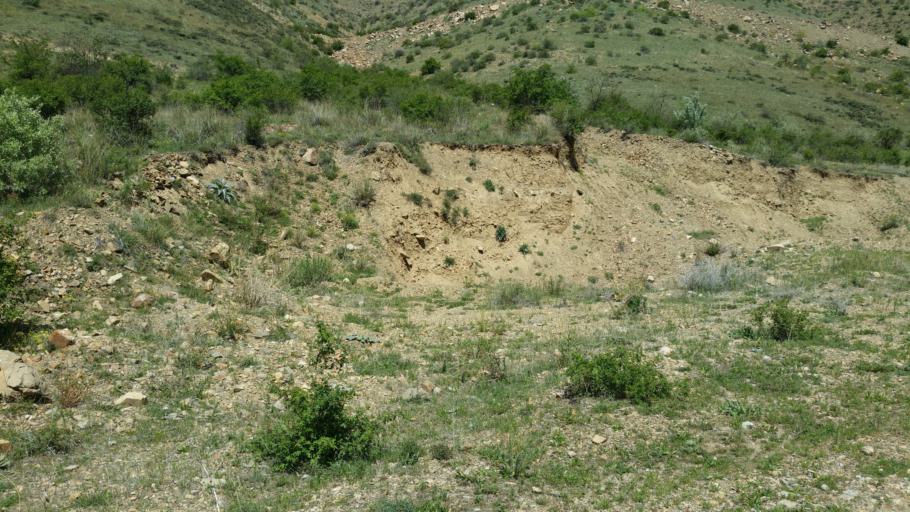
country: AM
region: Vayots' Dzori Marz
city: Vernashen
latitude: 39.7998
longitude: 45.3649
